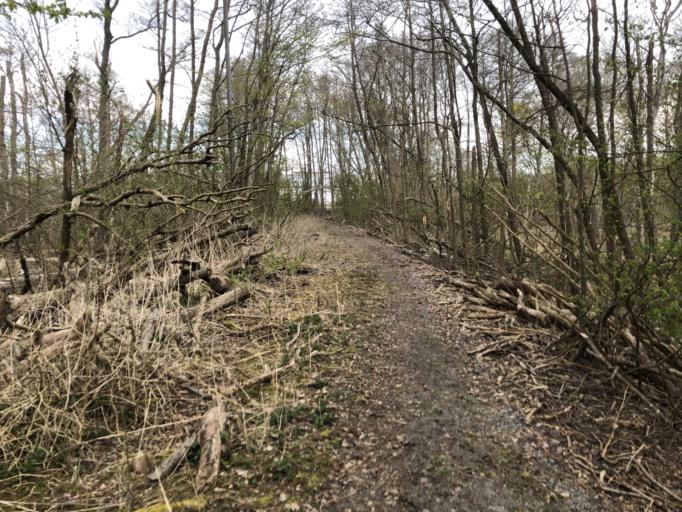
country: SE
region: Skane
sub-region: Malmo
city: Oxie
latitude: 55.5542
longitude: 13.0543
